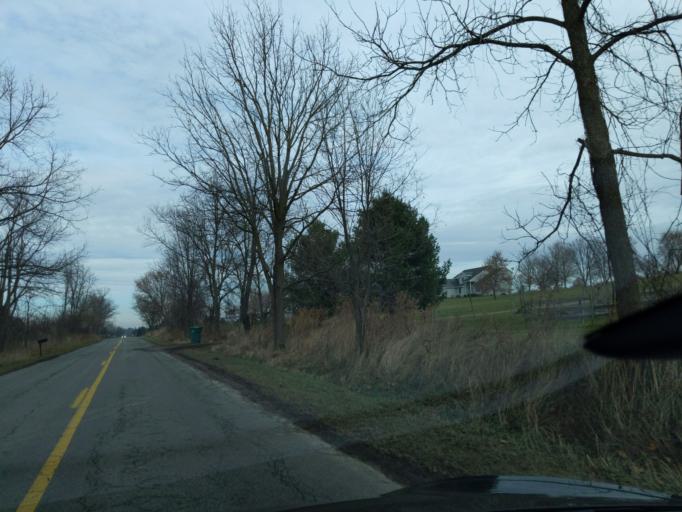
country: US
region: Michigan
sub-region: Ingham County
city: Leslie
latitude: 42.5038
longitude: -84.5024
